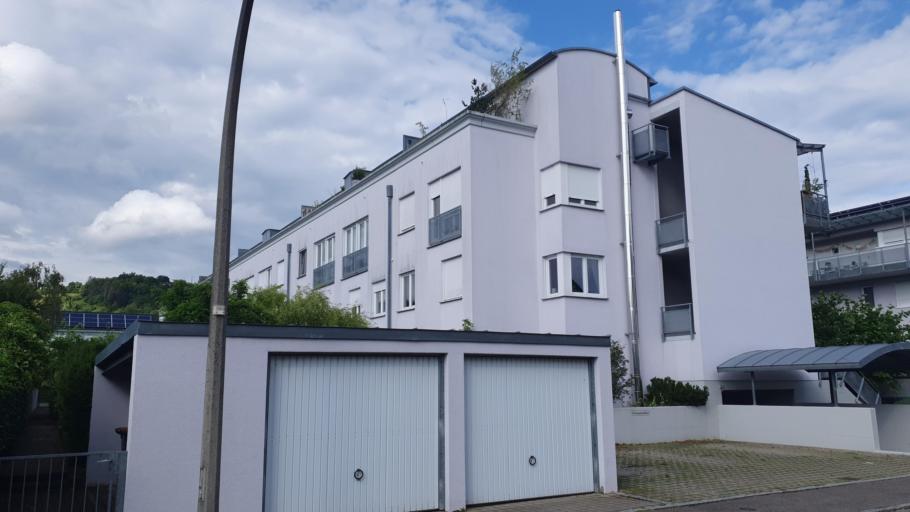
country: DE
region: Baden-Wuerttemberg
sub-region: Freiburg Region
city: Weil am Rhein
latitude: 47.5913
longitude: 7.6316
